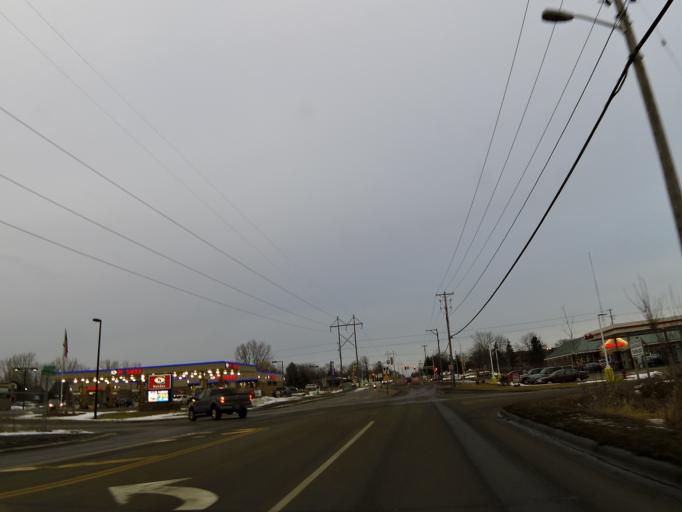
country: US
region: Minnesota
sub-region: Ramsey County
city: North Saint Paul
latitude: 44.9961
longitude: -92.9644
